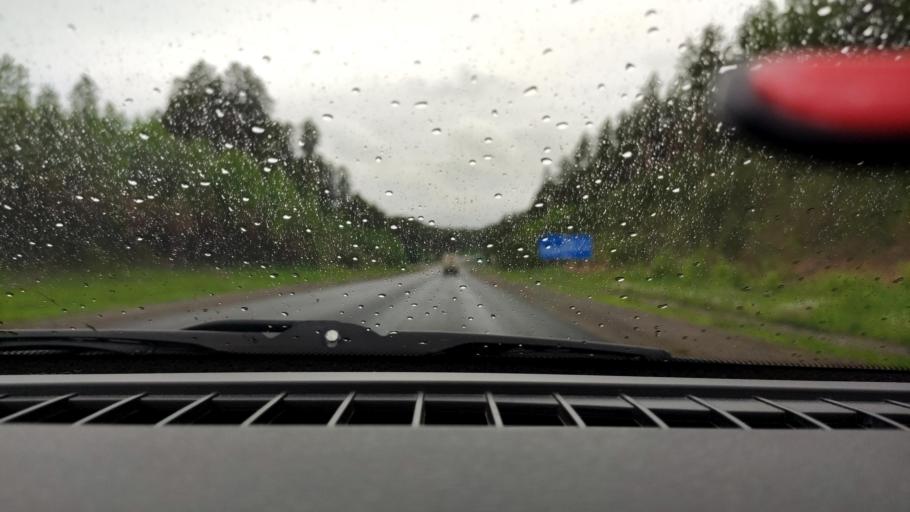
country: RU
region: Perm
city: Karagay
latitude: 58.2566
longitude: 54.8928
